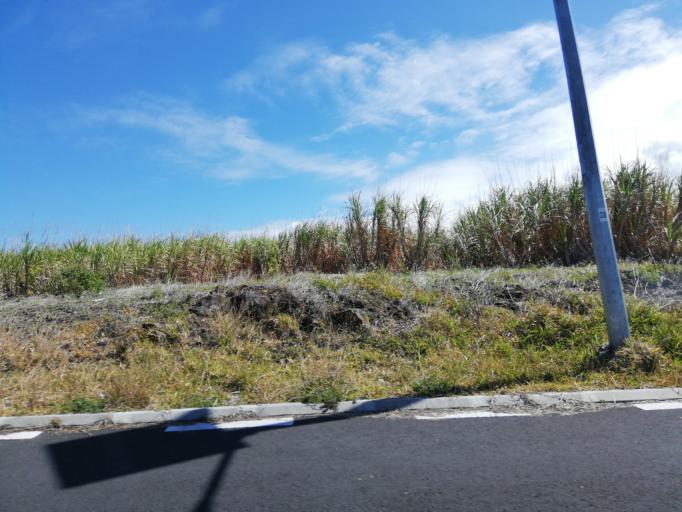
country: MU
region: Grand Port
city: Plaine Magnien
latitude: -20.4509
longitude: 57.6937
